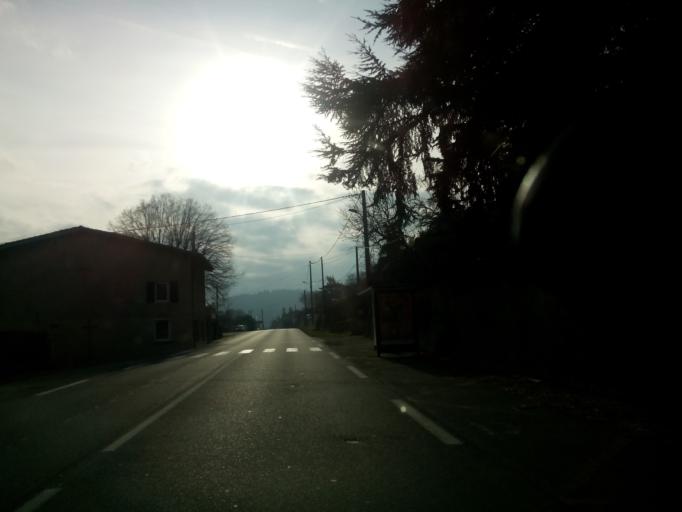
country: FR
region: Rhone-Alpes
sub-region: Departement de la Loire
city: Chavanay
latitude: 45.4097
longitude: 4.7365
